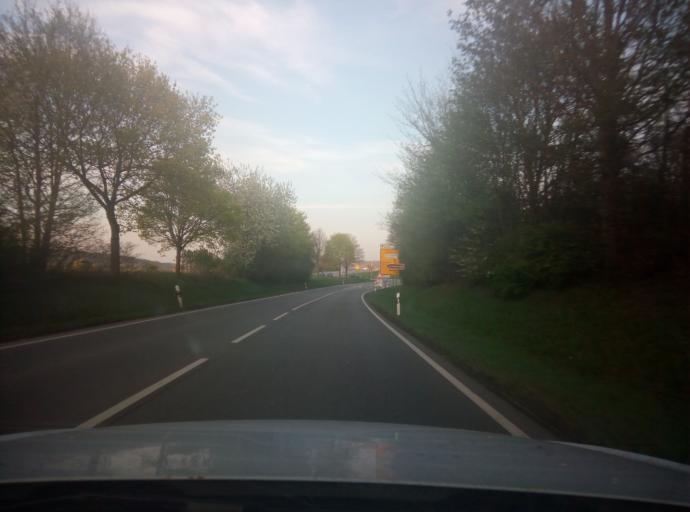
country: DE
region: Baden-Wuerttemberg
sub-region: Tuebingen Region
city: Rottenburg
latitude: 48.4880
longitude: 8.9459
